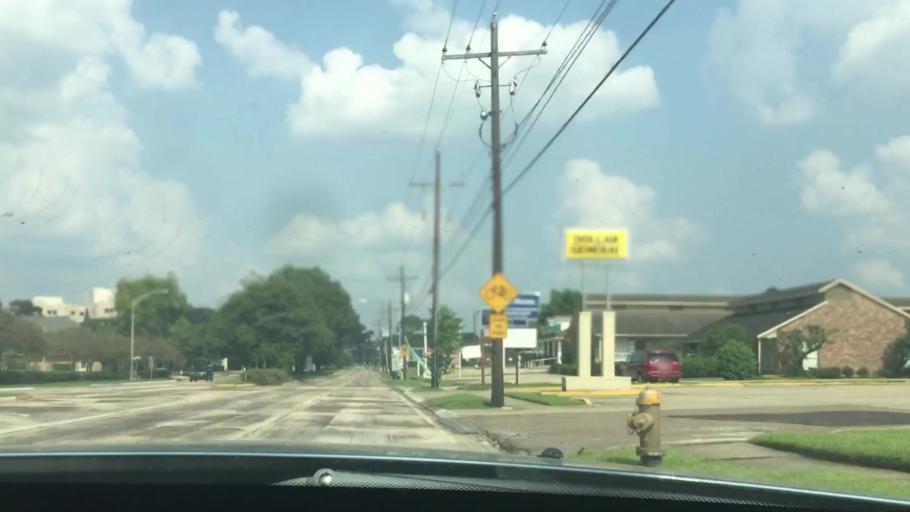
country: US
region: Louisiana
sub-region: East Baton Rouge Parish
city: Westminster
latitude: 30.4424
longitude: -91.1039
